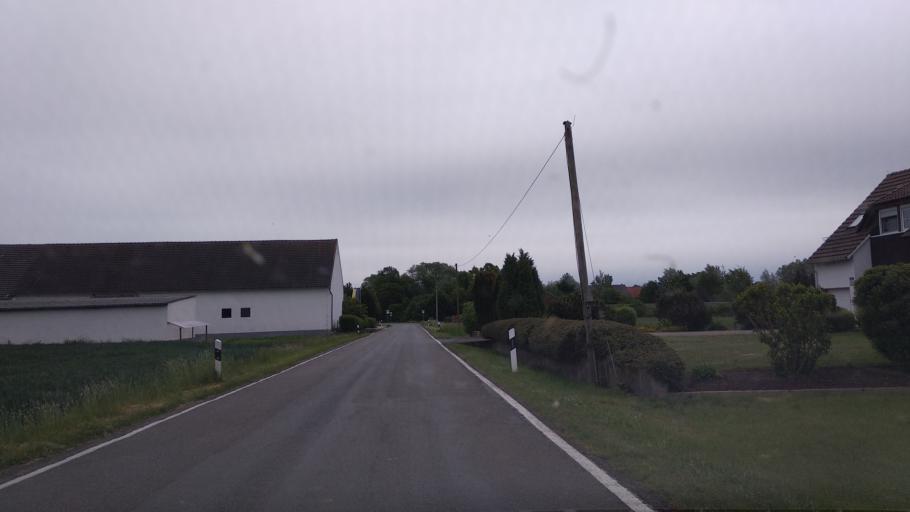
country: DE
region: North Rhine-Westphalia
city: Borgentreich
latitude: 51.5446
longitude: 9.1996
